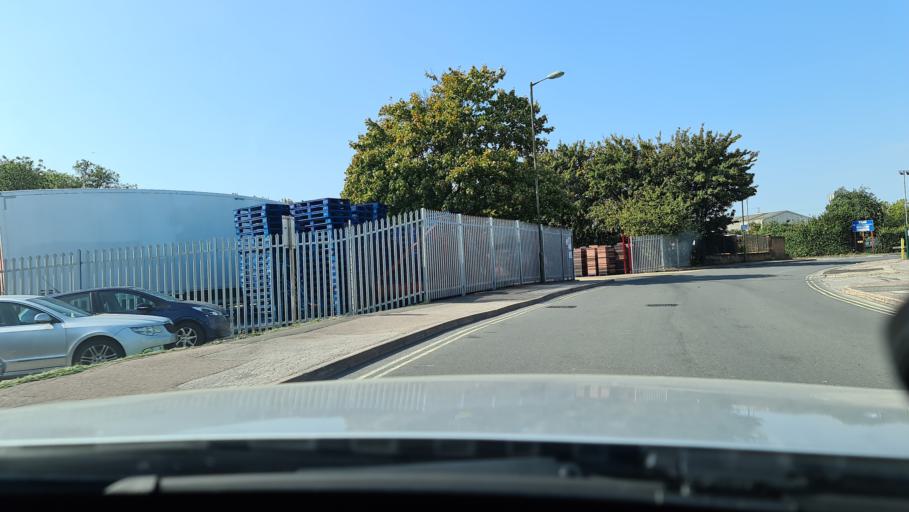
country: GB
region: England
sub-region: Oxfordshire
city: Banbury
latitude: 52.0728
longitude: -1.3241
